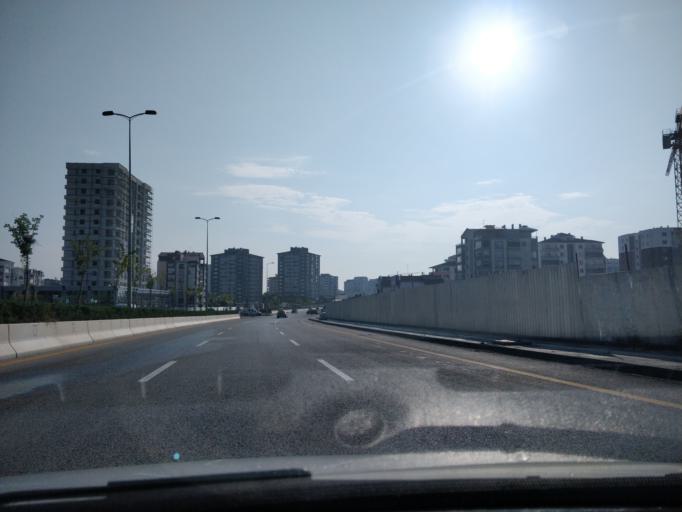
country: TR
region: Ankara
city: Etimesgut
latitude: 39.8966
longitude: 32.6363
